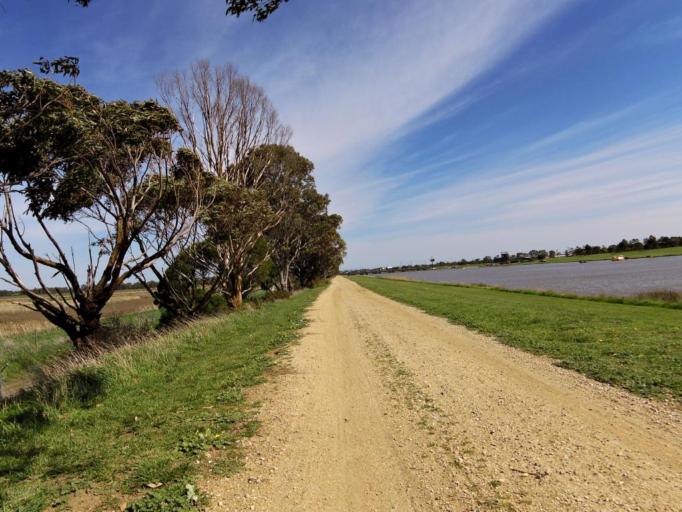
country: AU
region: Victoria
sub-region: Kingston
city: Patterson Lakes
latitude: -38.0548
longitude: 145.1558
